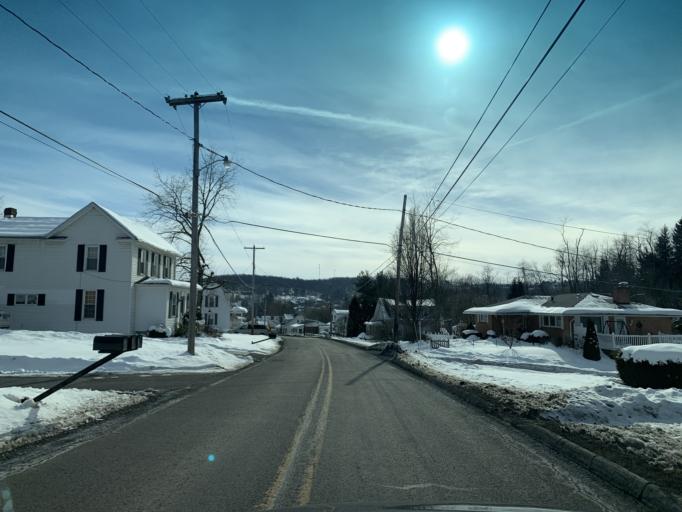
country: US
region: Maryland
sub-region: Allegany County
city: Frostburg
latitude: 39.6576
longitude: -78.8961
